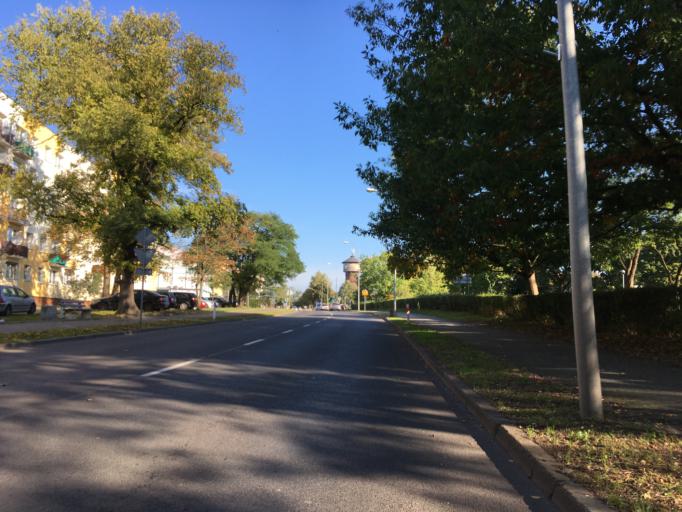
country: PL
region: Lubusz
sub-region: Powiat gorzowski
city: Kostrzyn nad Odra
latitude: 52.5880
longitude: 14.6503
